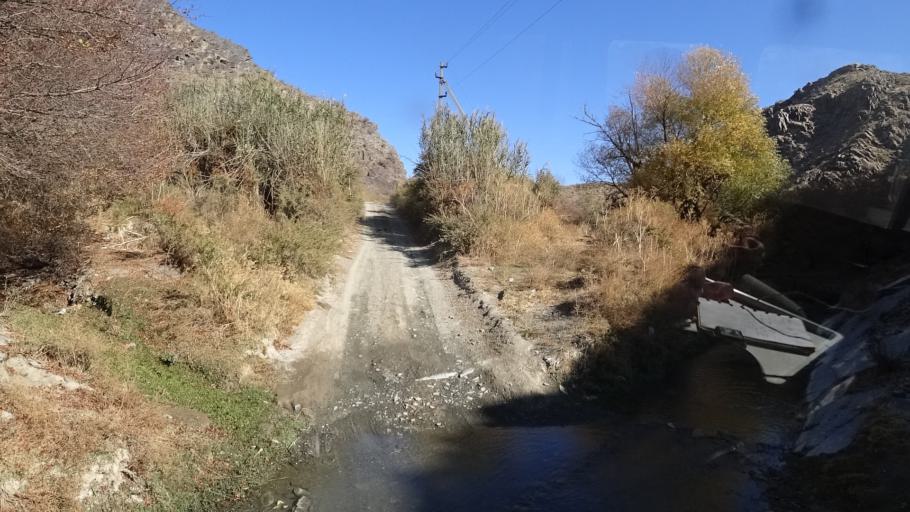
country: UZ
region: Navoiy
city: Nurota
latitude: 40.3098
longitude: 65.6215
